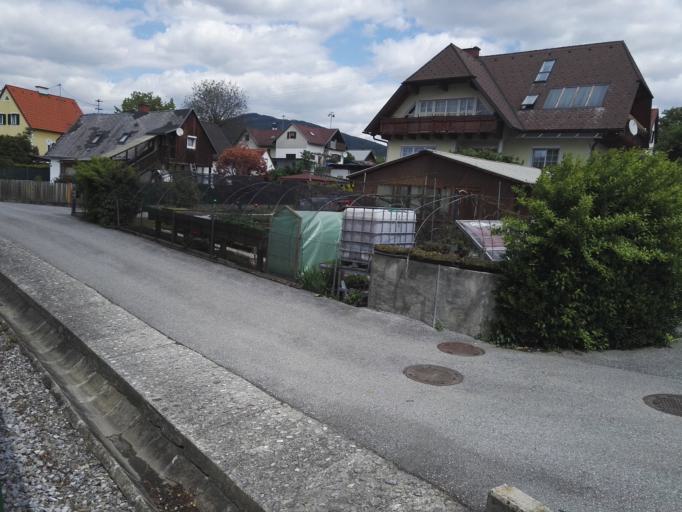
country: AT
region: Styria
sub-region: Politischer Bezirk Weiz
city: Krottendorf
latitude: 47.2131
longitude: 15.6397
